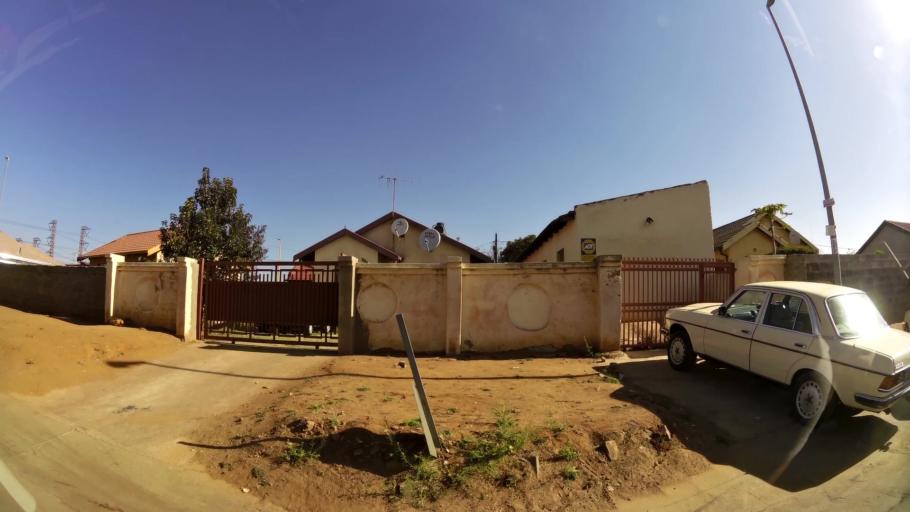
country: ZA
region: Gauteng
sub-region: Ekurhuleni Metropolitan Municipality
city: Tembisa
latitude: -26.0208
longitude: 28.2347
